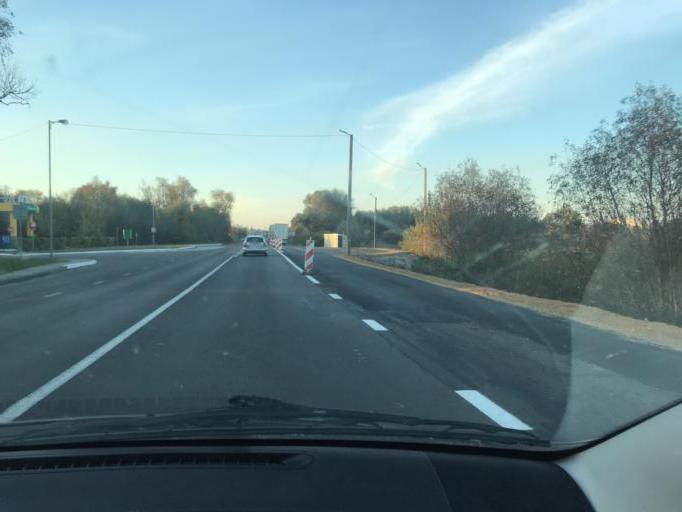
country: BY
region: Brest
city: Pinsk
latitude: 52.1036
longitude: 26.1117
